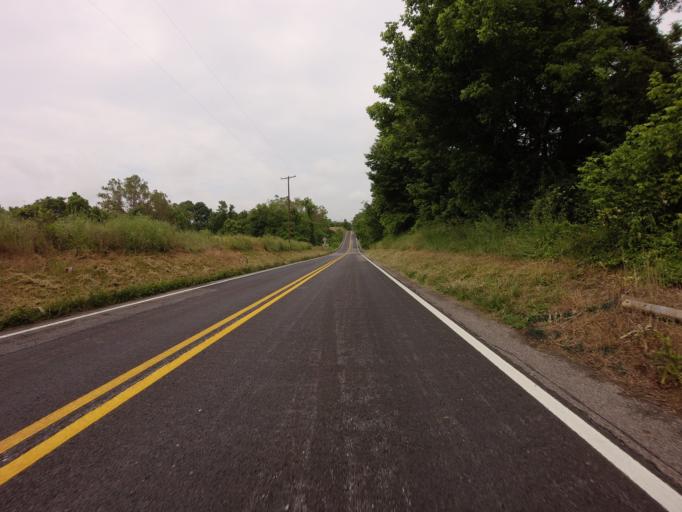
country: US
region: Maryland
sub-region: Frederick County
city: Brunswick
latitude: 39.3265
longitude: -77.5851
